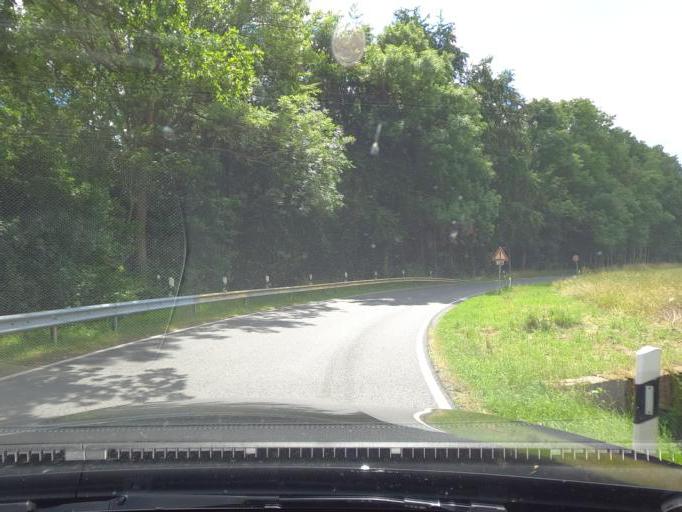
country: DE
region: Lower Saxony
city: Elbe
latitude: 52.1127
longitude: 10.2770
